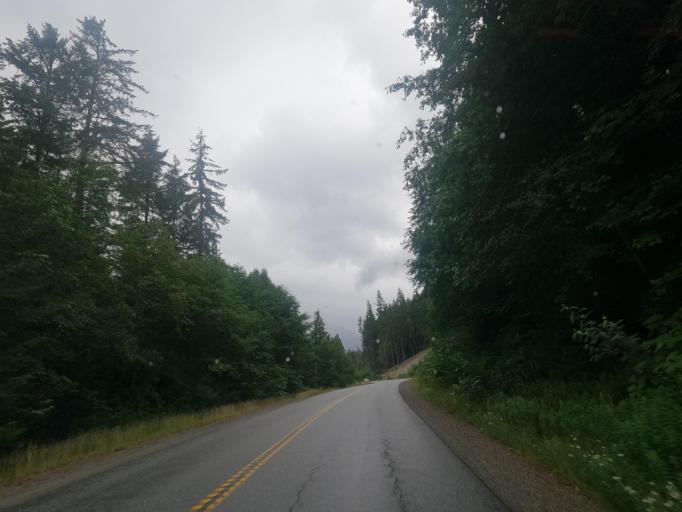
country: CA
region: British Columbia
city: Pemberton
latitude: 50.3246
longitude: -122.5576
